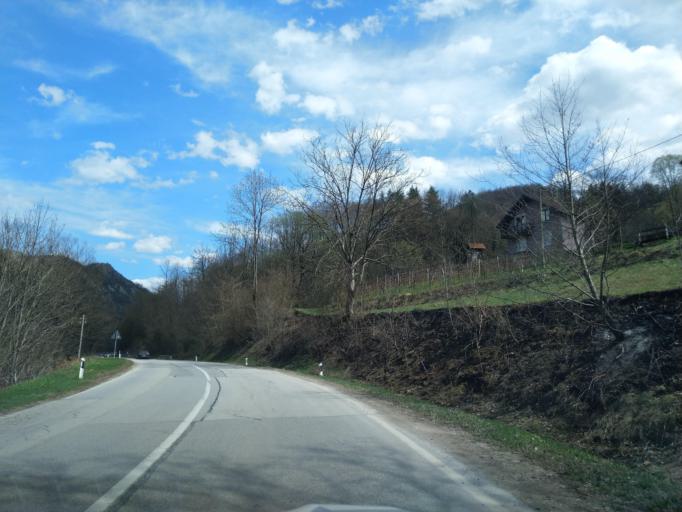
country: RS
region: Central Serbia
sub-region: Zlatiborski Okrug
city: Arilje
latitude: 43.6625
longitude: 20.0987
